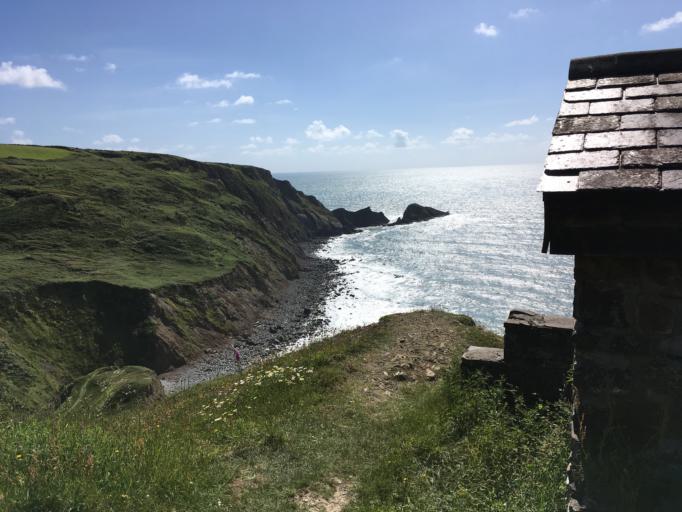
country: GB
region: England
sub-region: Cornwall
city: Flexbury
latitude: 50.9299
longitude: -4.5440
